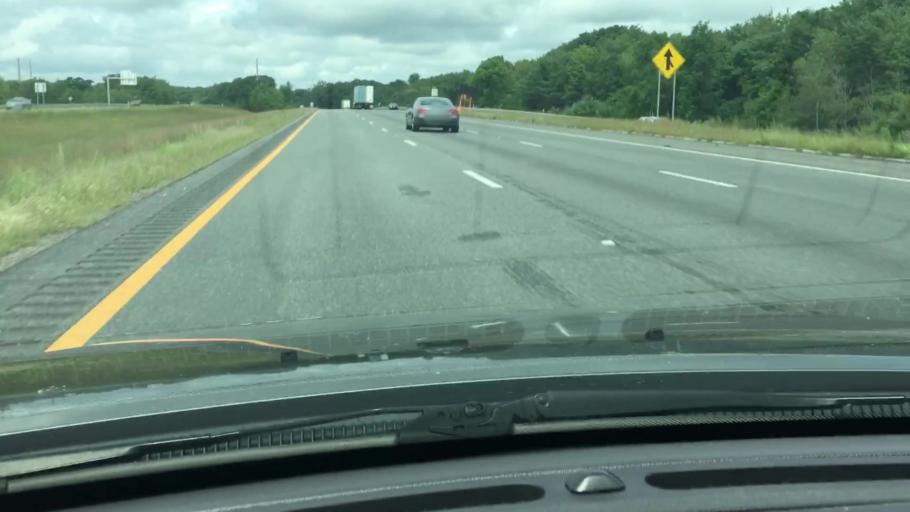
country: US
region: Massachusetts
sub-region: Worcester County
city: Milford
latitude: 42.1488
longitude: -71.4847
